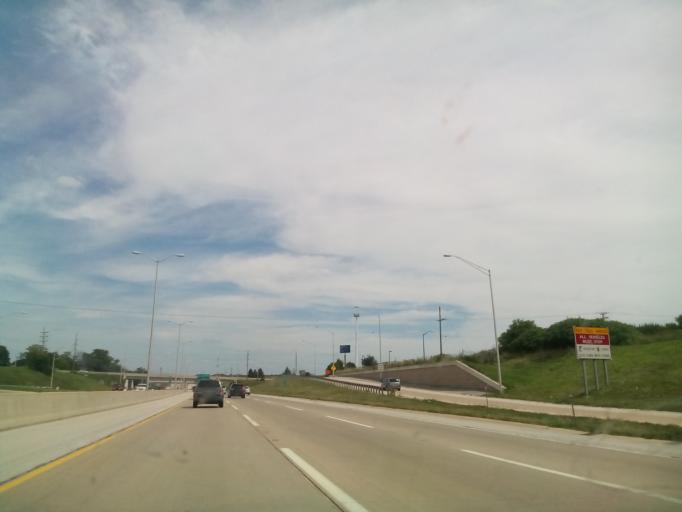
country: US
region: Illinois
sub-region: Kane County
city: North Aurora
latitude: 41.7955
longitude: -88.3319
